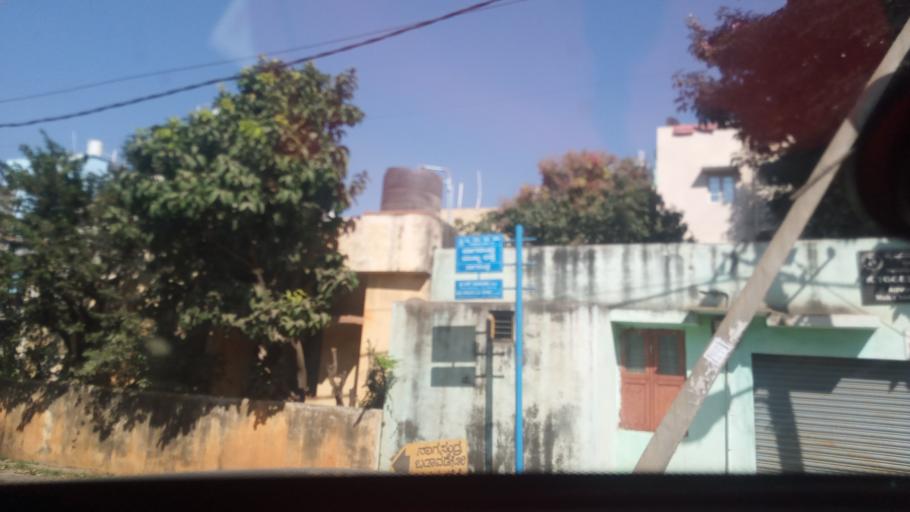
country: IN
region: Karnataka
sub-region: Bangalore Urban
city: Yelahanka
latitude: 13.0405
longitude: 77.5014
